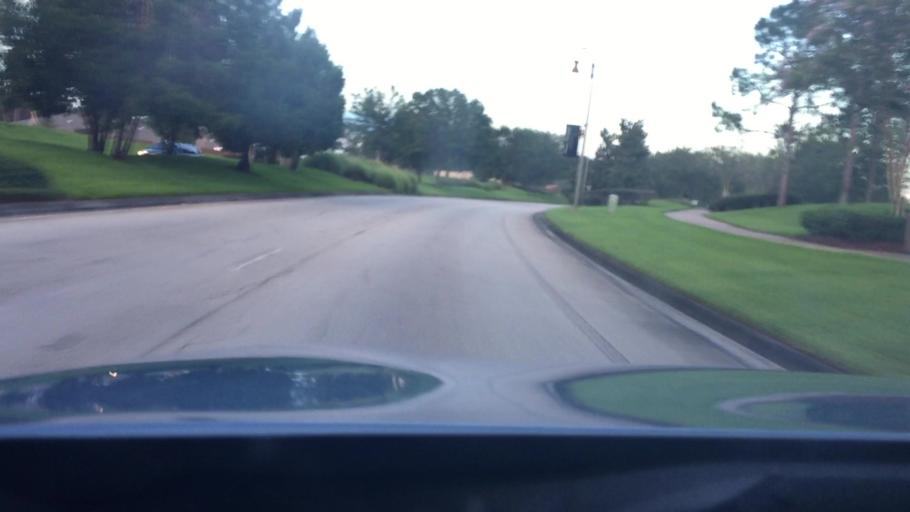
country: US
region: Florida
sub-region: Osceola County
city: Saint Cloud
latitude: 28.2280
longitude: -81.3041
